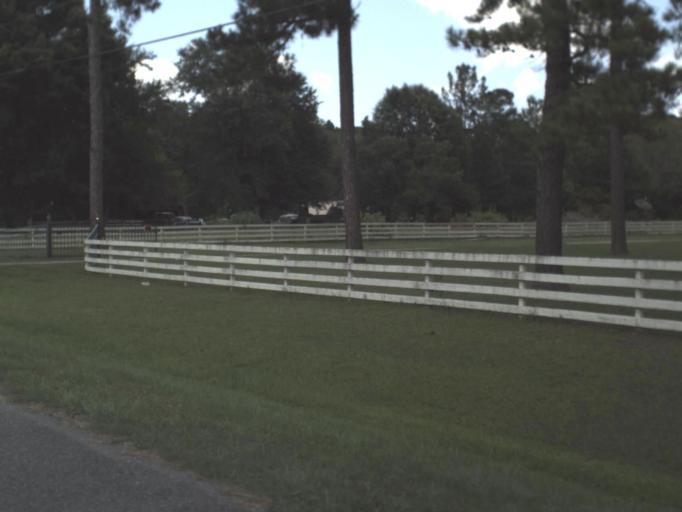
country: US
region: Florida
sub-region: Baker County
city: Macclenny
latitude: 30.3384
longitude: -82.1252
